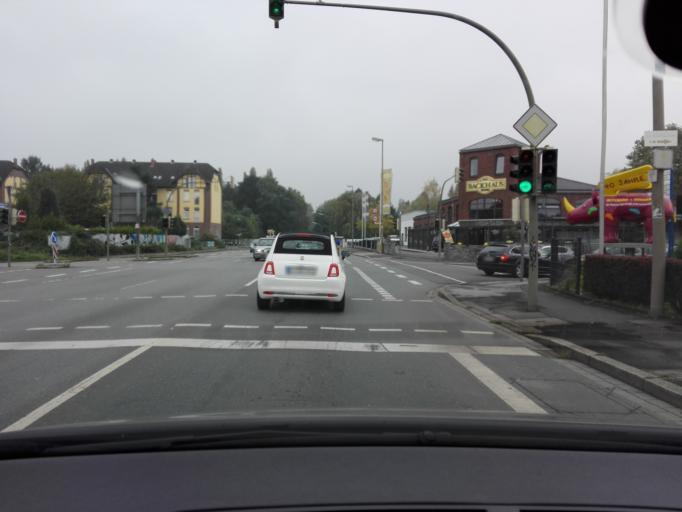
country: DE
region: North Rhine-Westphalia
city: Lanstrop
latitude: 51.5371
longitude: 7.5413
